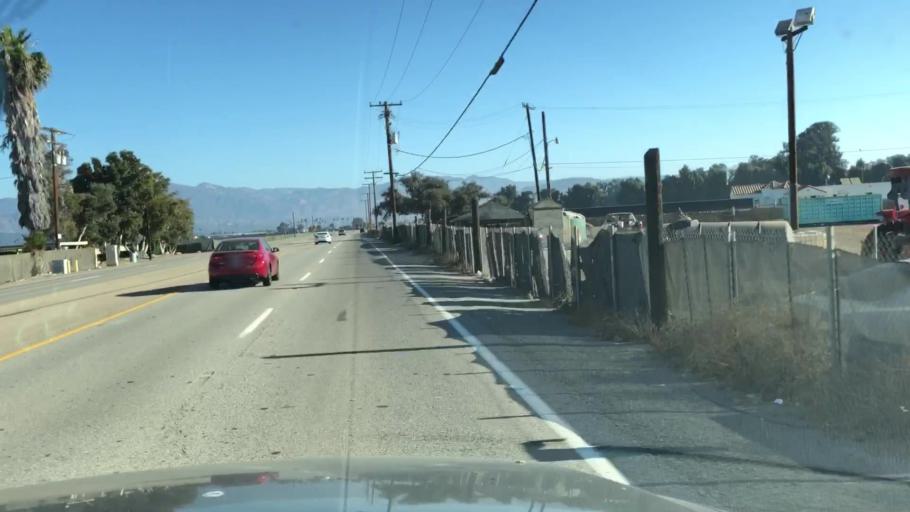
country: US
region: California
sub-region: Ventura County
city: El Rio
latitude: 34.2415
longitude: -119.1508
